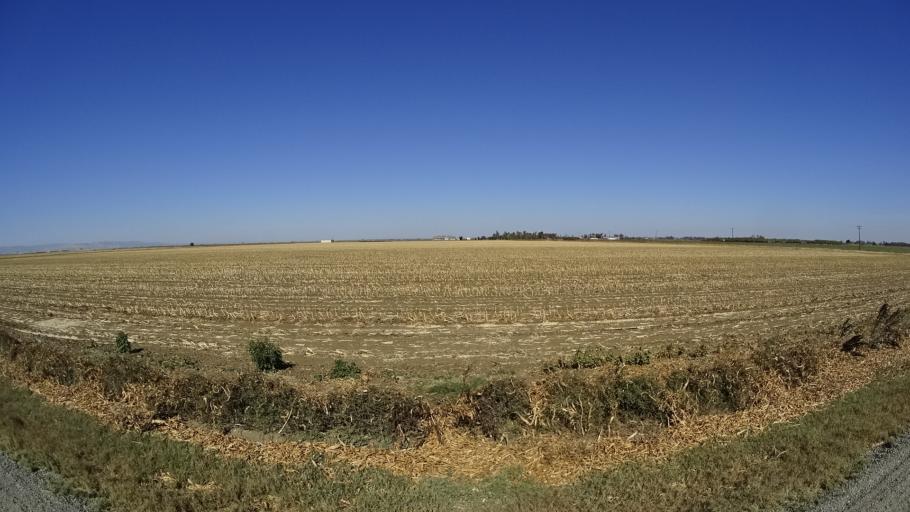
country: US
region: California
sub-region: Yolo County
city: Cottonwood
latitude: 38.6199
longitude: -121.8969
